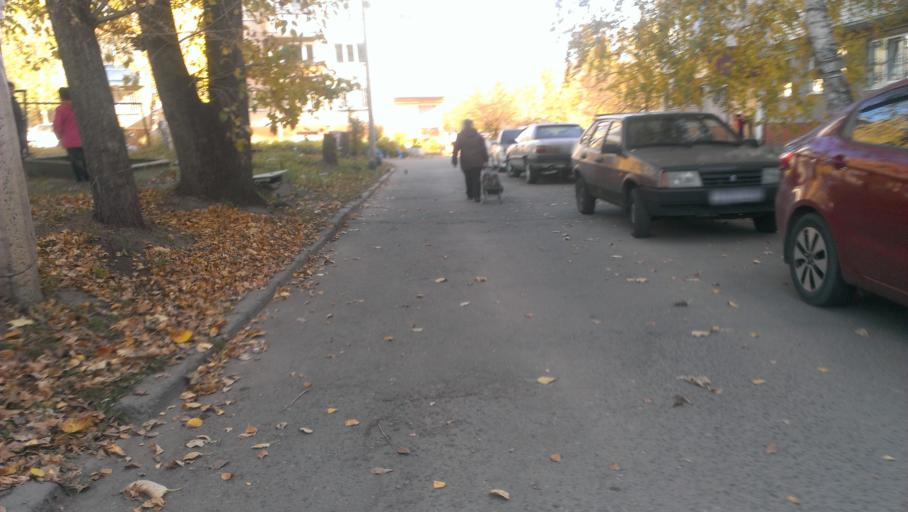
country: RU
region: Altai Krai
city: Novosilikatnyy
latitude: 53.3511
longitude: 83.6852
